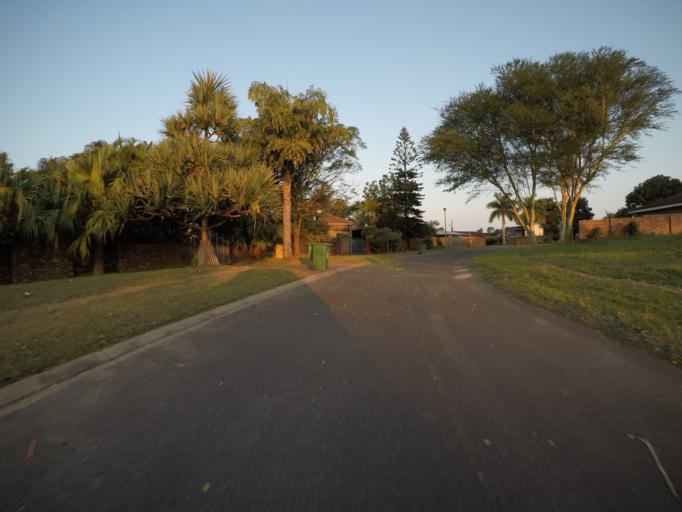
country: ZA
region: KwaZulu-Natal
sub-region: uThungulu District Municipality
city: Richards Bay
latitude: -28.7648
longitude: 32.1216
